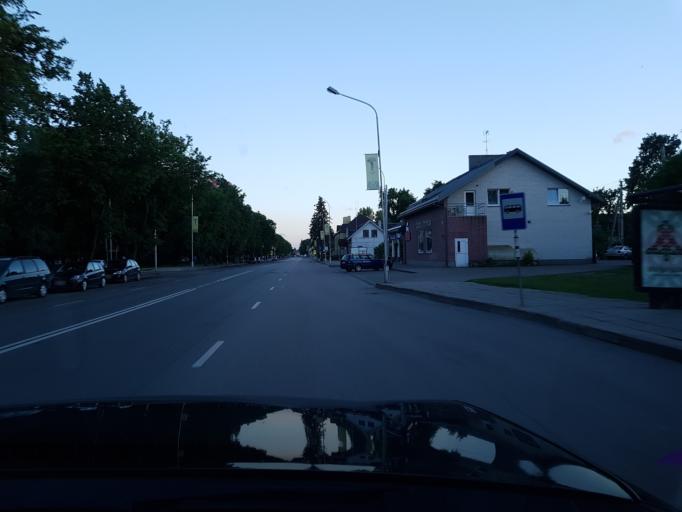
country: LT
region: Marijampoles apskritis
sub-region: Marijampole Municipality
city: Marijampole
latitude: 54.5662
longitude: 23.3582
